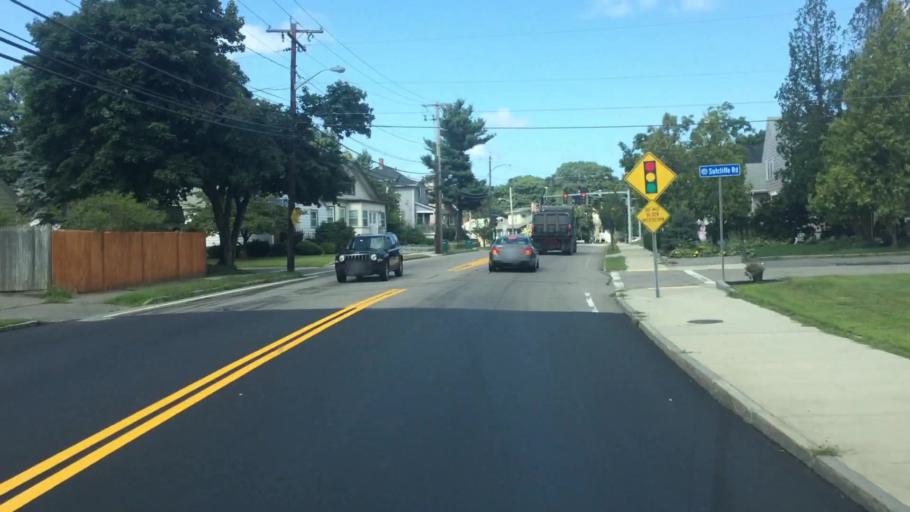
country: US
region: Massachusetts
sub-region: Essex County
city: South Peabody
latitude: 42.4954
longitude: -70.9706
